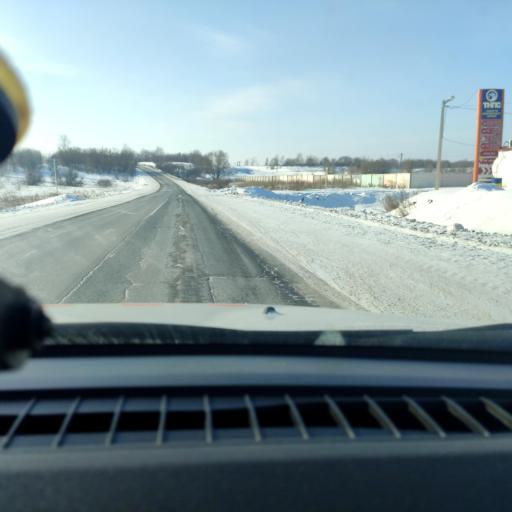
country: RU
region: Samara
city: Smyshlyayevka
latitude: 53.1562
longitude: 50.4102
